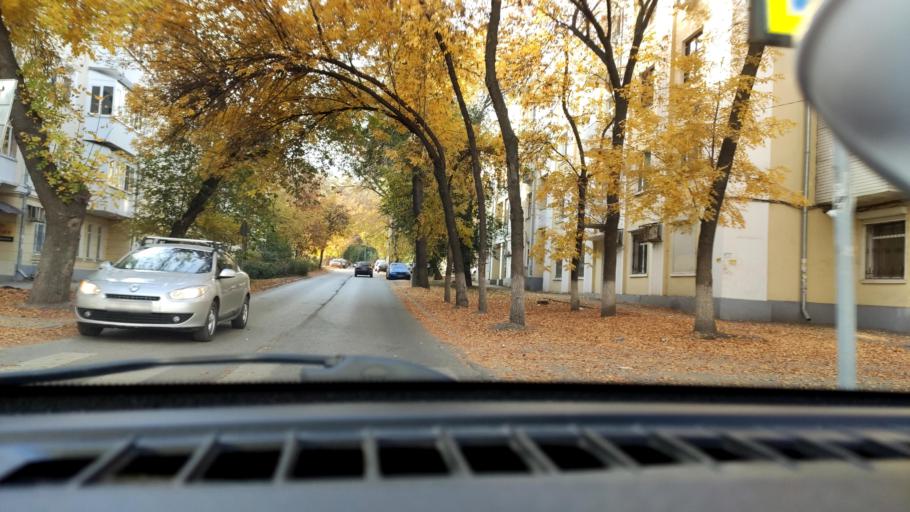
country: RU
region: Samara
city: Samara
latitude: 53.2197
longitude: 50.1604
